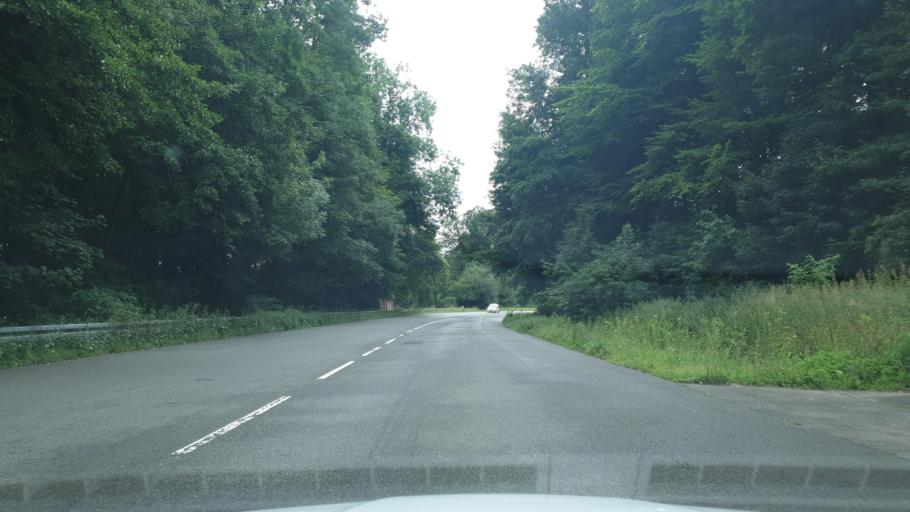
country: DE
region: Lower Saxony
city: Bissendorf
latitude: 52.2058
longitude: 8.1259
